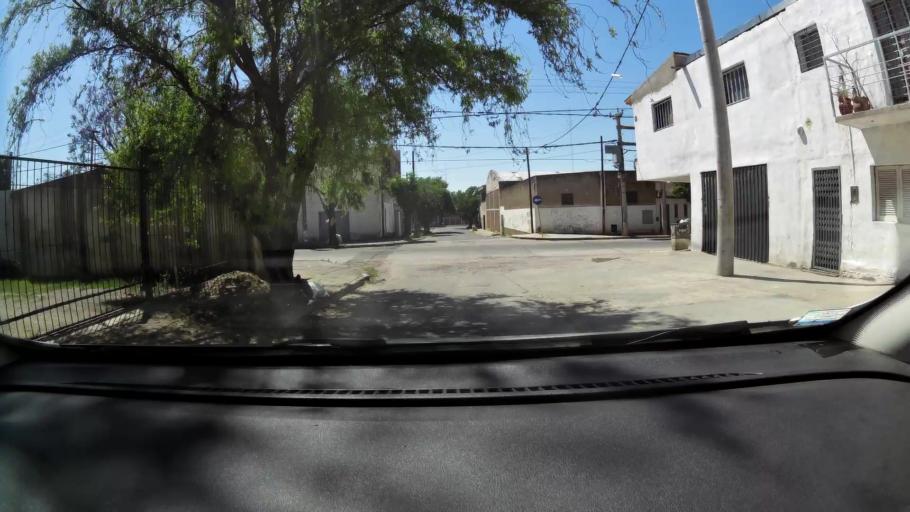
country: AR
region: Cordoba
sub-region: Departamento de Capital
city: Cordoba
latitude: -31.4280
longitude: -64.2031
